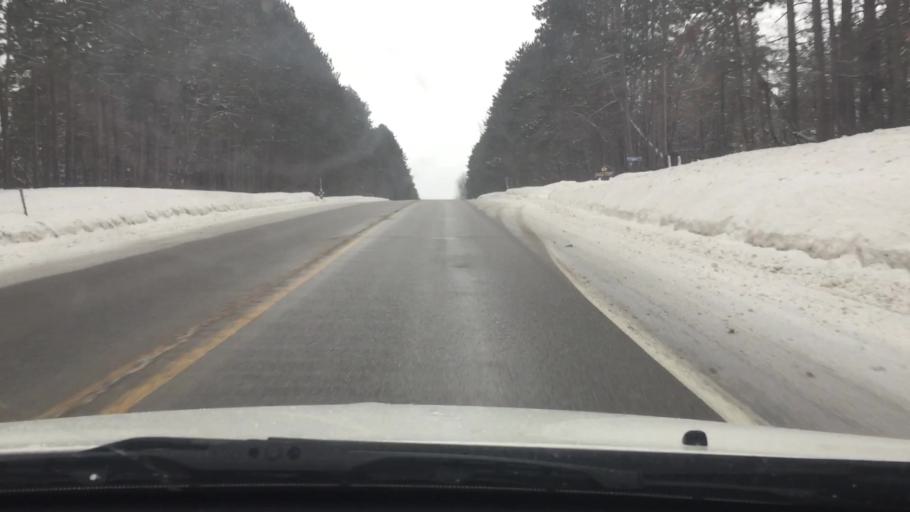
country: US
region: Michigan
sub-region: Otsego County
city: Gaylord
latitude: 45.0618
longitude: -84.8068
